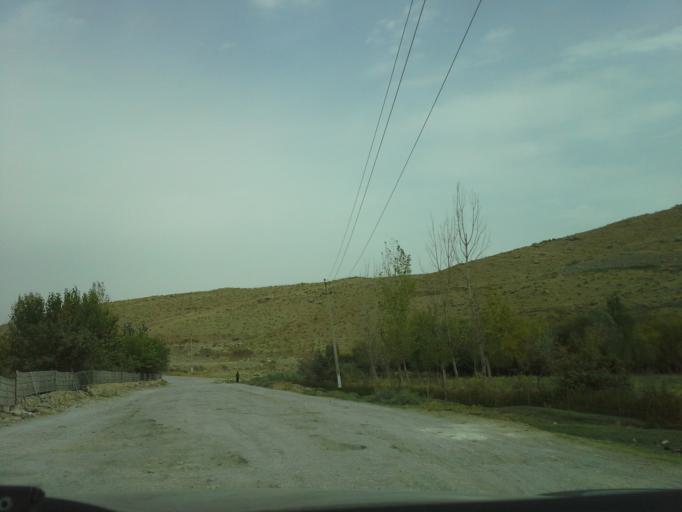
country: UZ
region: Qashqadaryo
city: Qorashina
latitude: 37.9187
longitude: 66.4864
